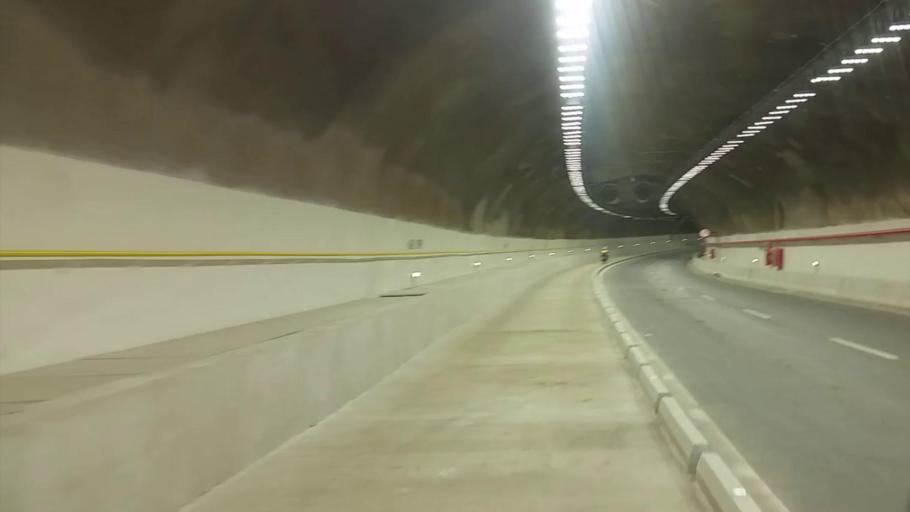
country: BR
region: Rio de Janeiro
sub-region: Nilopolis
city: Nilopolis
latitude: -22.8909
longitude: -43.4007
